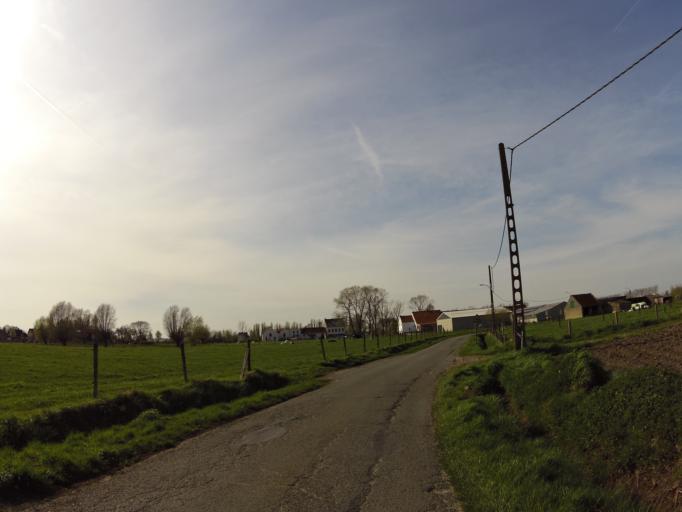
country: BE
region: Flanders
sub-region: Provincie West-Vlaanderen
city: Oudenburg
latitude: 51.1454
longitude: 3.0289
